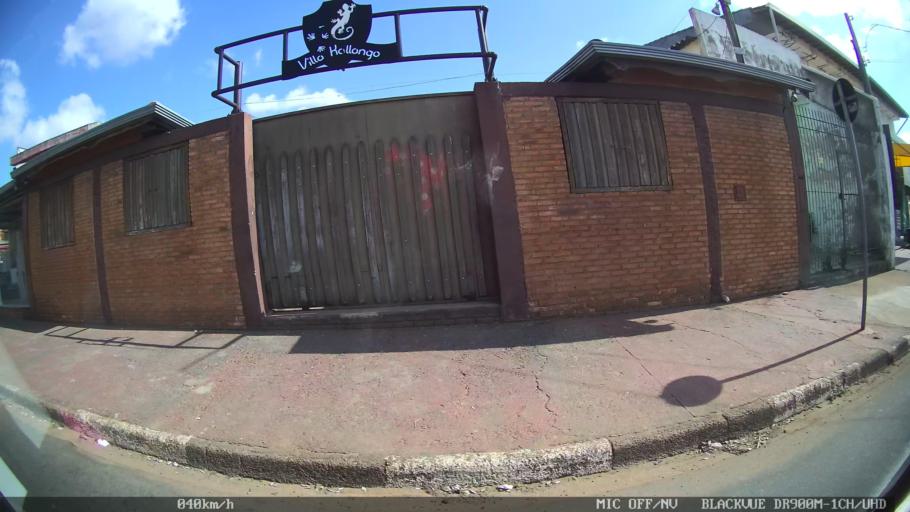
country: BR
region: Sao Paulo
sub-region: Hortolandia
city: Hortolandia
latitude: -22.8817
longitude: -47.2011
